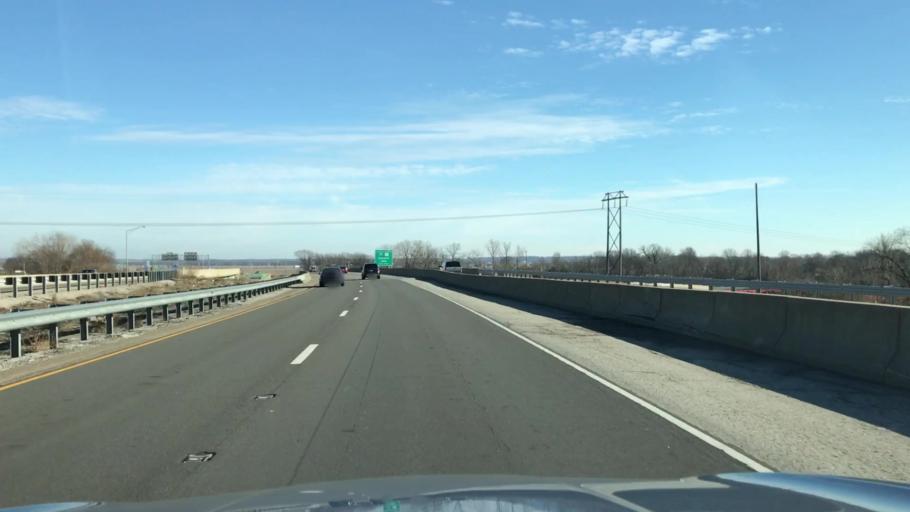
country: US
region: Illinois
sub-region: Madison County
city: Mitchell
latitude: 38.7580
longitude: -90.0897
